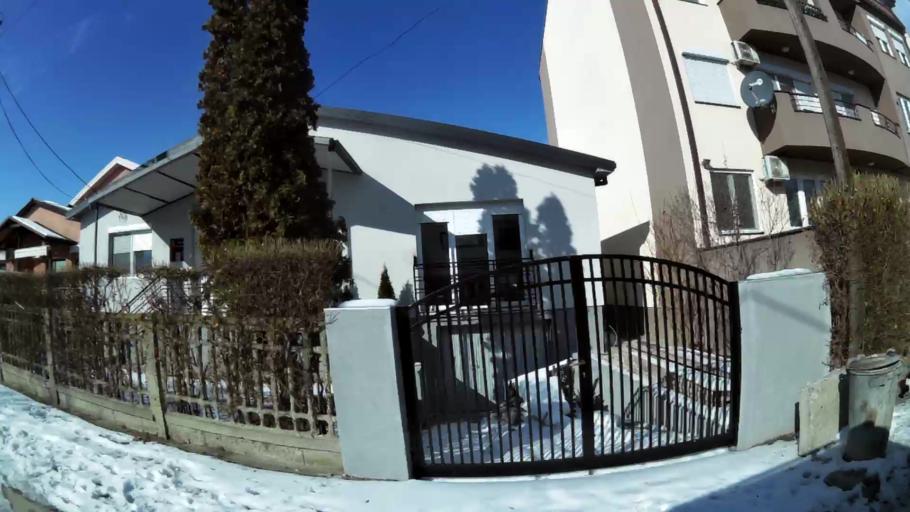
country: MK
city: Krushopek
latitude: 42.0014
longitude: 21.3723
